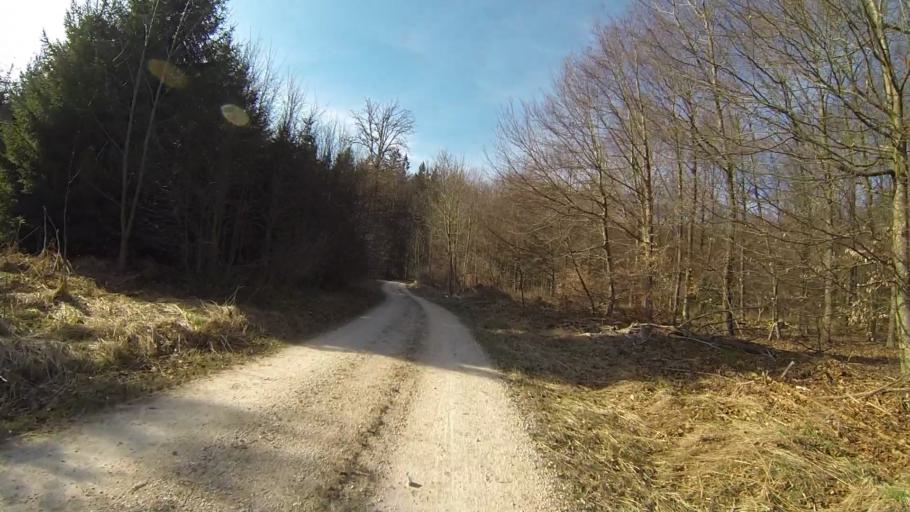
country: DE
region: Baden-Wuerttemberg
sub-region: Regierungsbezirk Stuttgart
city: Niederstotzingen
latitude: 48.5656
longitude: 10.2269
